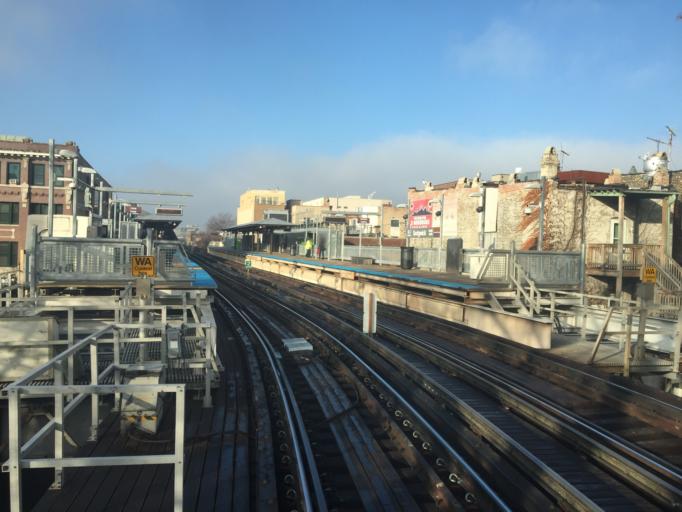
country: US
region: Illinois
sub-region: Cook County
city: Chicago
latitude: 41.9104
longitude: -87.6380
